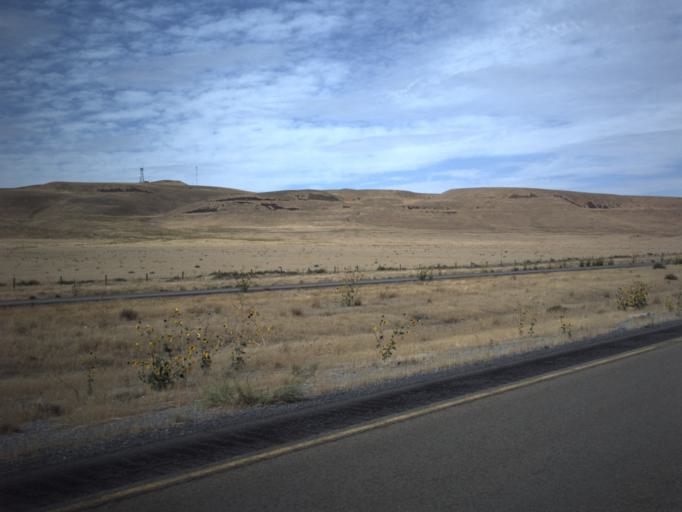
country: US
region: Utah
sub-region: Tooele County
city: Grantsville
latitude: 40.8051
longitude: -112.8583
